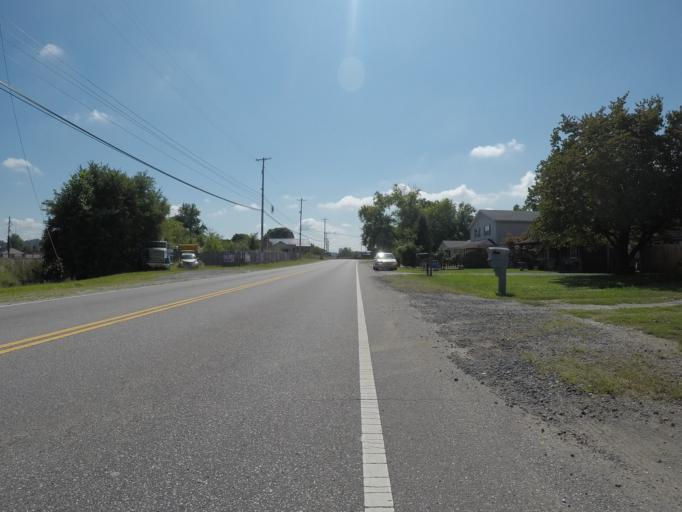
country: US
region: Ohio
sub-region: Lawrence County
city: South Point
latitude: 38.4215
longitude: -82.5894
